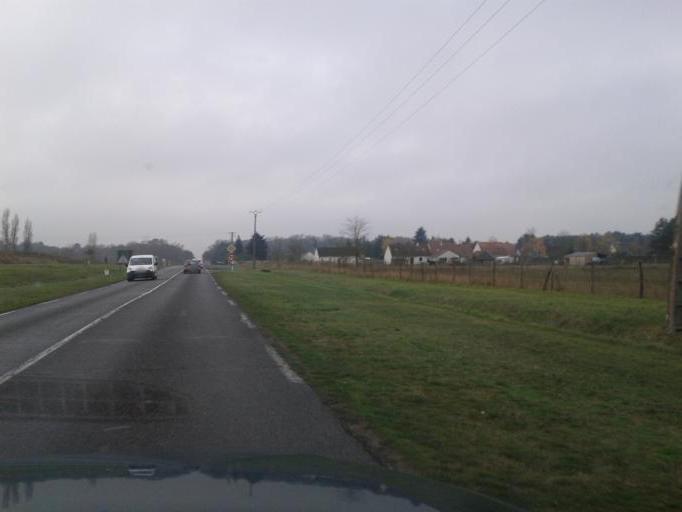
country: FR
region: Centre
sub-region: Departement du Loiret
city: Dry
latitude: 47.7900
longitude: 1.7162
